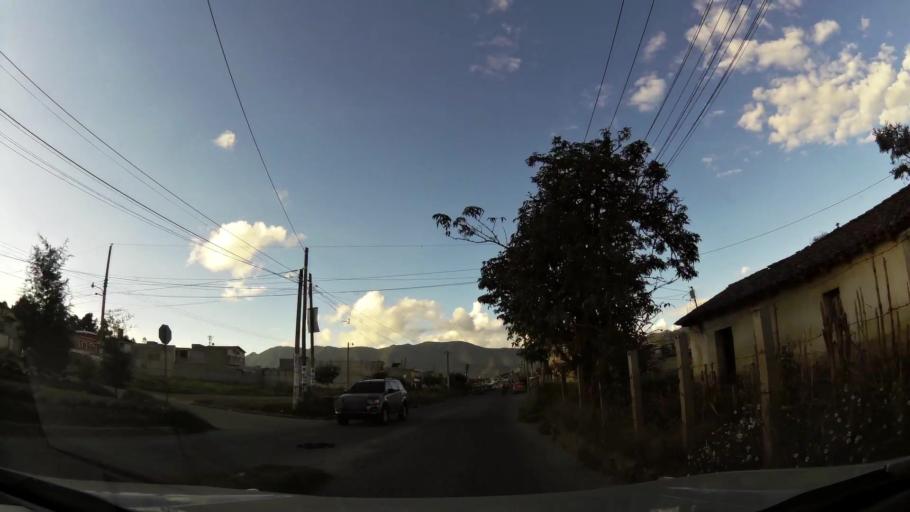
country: GT
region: Quetzaltenango
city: Quetzaltenango
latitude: 14.8590
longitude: -91.5354
